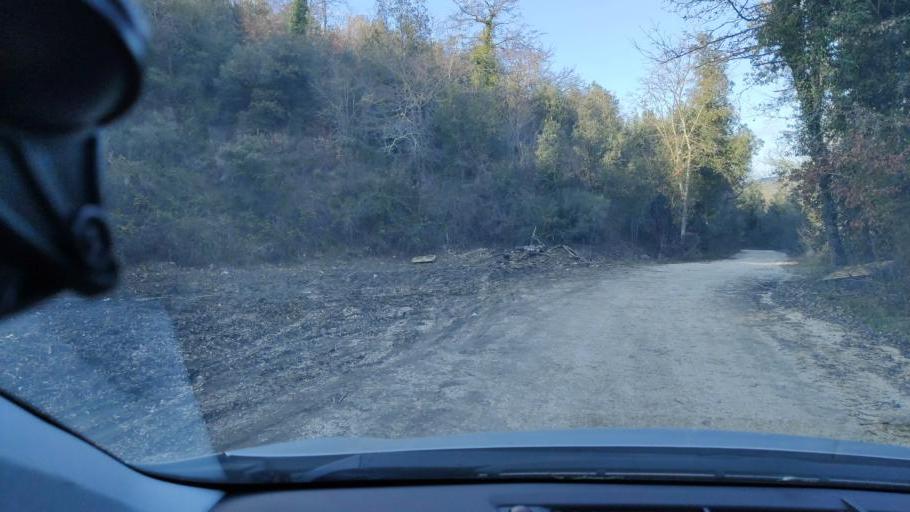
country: IT
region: Umbria
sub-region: Provincia di Terni
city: Amelia
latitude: 42.5639
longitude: 12.4395
